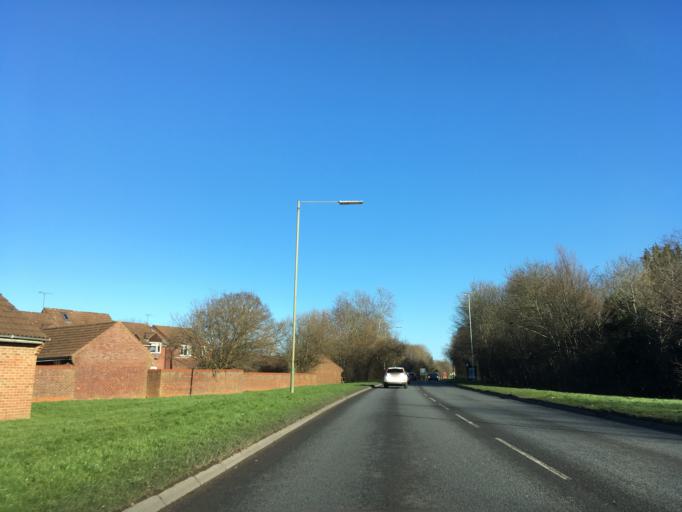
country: GB
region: England
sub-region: Wiltshire
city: Lydiard Tregoze
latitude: 51.5566
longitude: -1.8371
